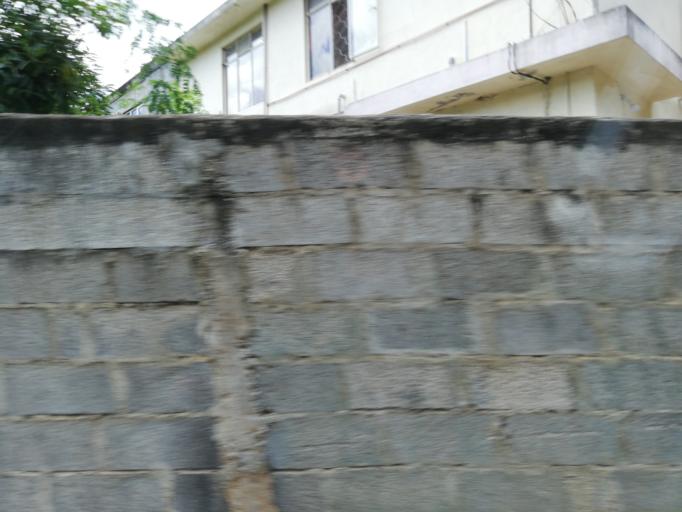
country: MU
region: Moka
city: Pailles
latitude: -20.1919
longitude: 57.4714
